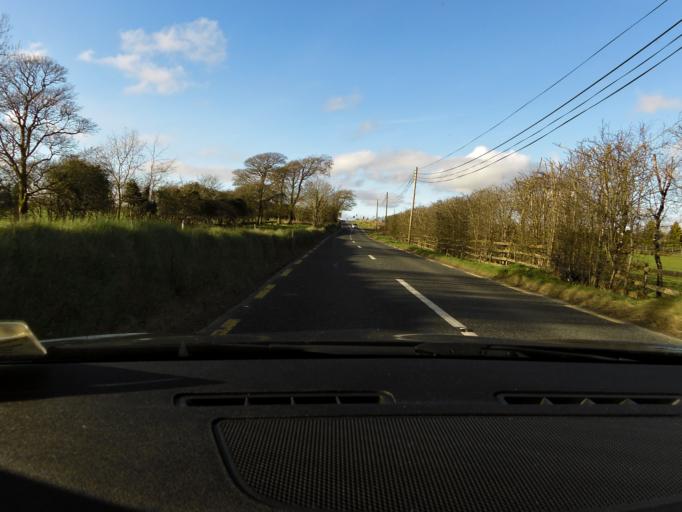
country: IE
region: Connaught
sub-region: Roscommon
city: Roscommon
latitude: 53.6585
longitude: -8.1982
